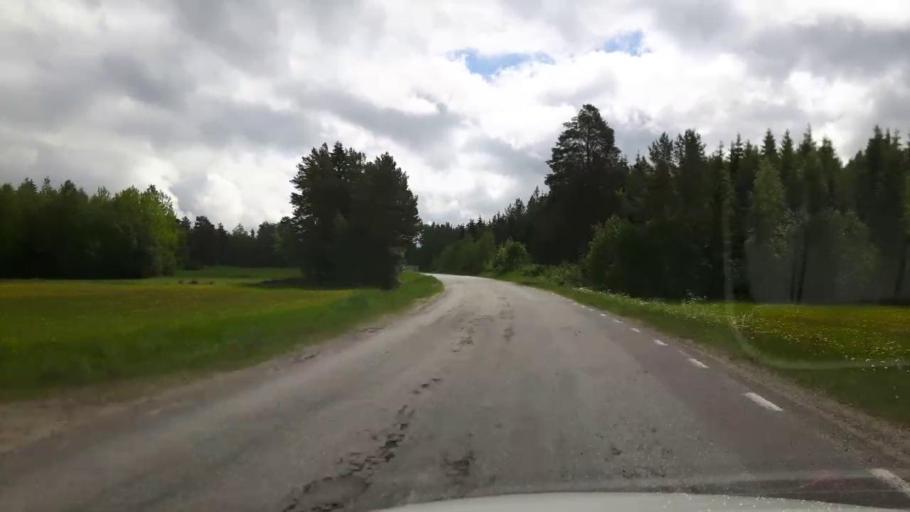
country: SE
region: Gaevleborg
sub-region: Ovanakers Kommun
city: Edsbyn
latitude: 61.3443
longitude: 15.9302
